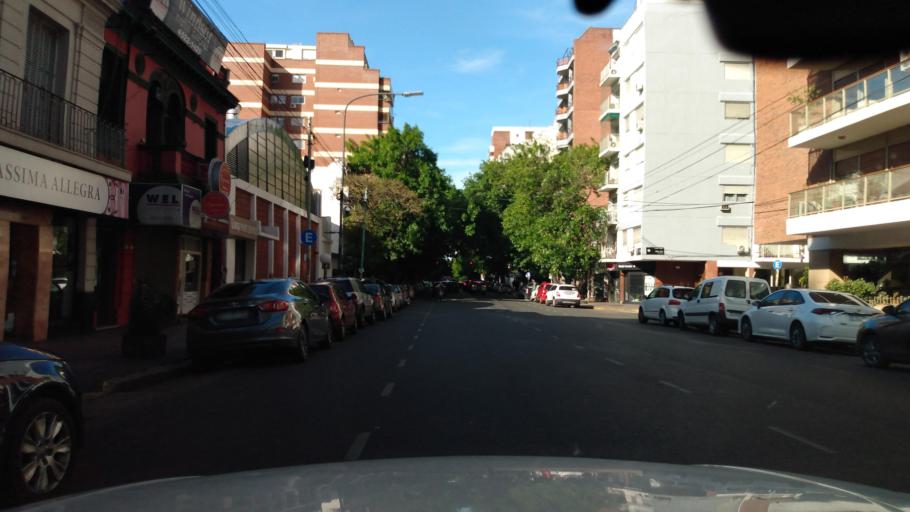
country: AR
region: Buenos Aires F.D.
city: Villa Santa Rita
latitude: -34.5779
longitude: -58.4883
